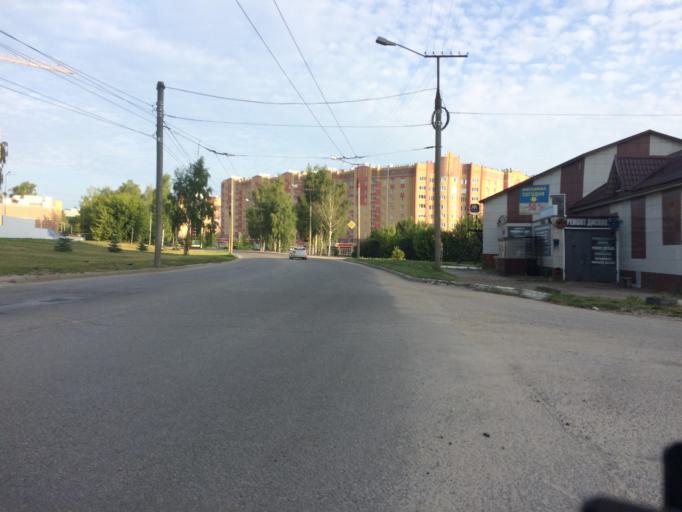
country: RU
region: Mariy-El
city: Yoshkar-Ola
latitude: 56.6405
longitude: 47.8589
